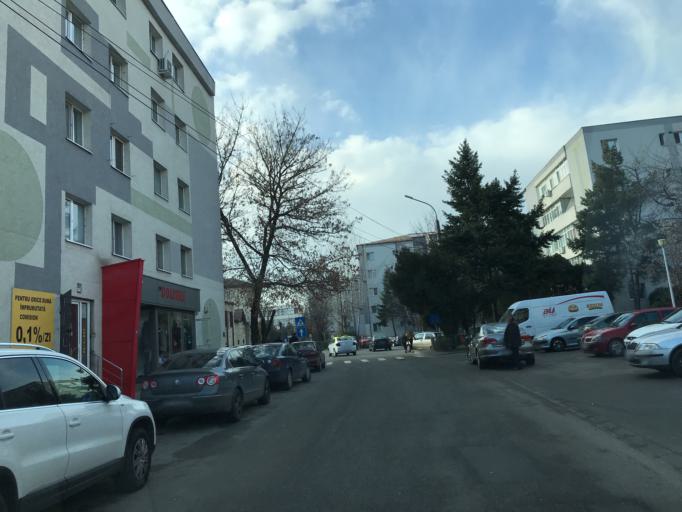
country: RO
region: Olt
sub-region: Municipiul Slatina
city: Slatina
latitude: 44.4267
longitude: 24.3673
